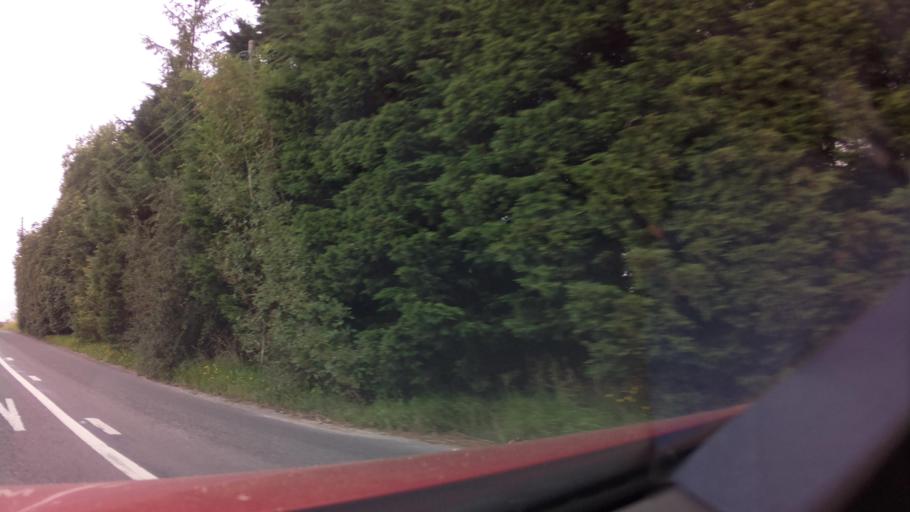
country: GB
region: England
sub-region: Staffordshire
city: Cheadle
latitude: 53.0309
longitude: -1.8892
